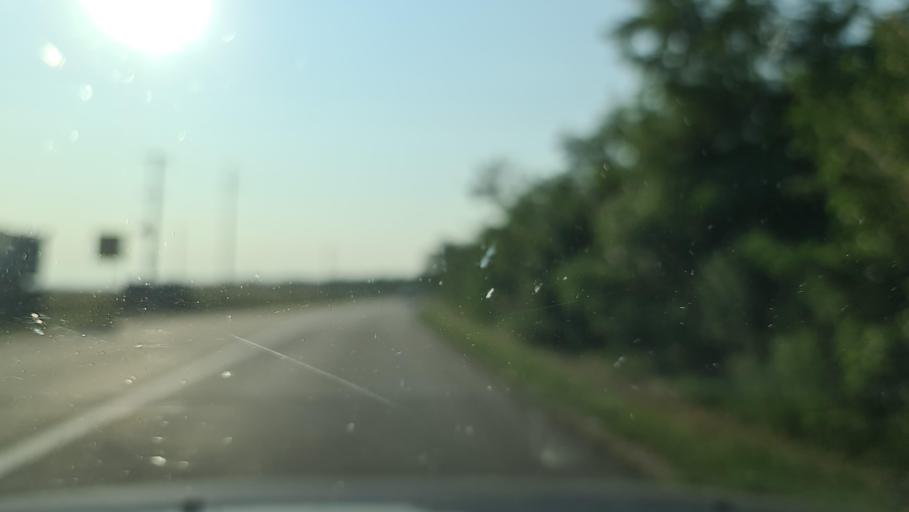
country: RO
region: Calarasi
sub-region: Comuna Dor Marunt
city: Dor Marunt
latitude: 44.4360
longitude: 26.9707
